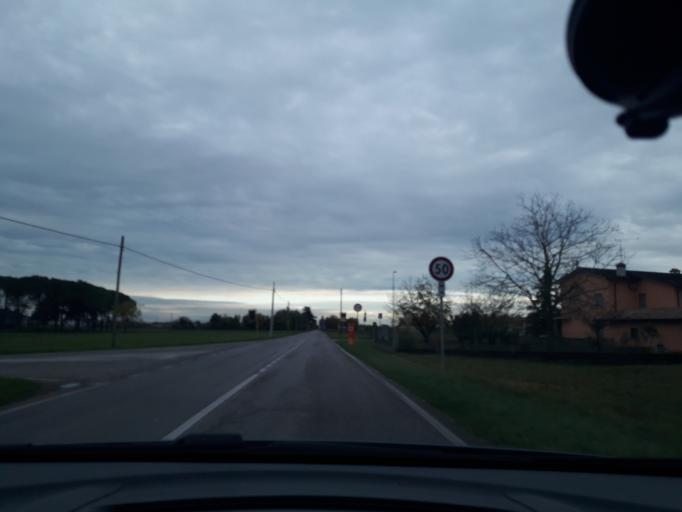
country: IT
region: Friuli Venezia Giulia
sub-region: Provincia di Udine
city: Tavagnacco
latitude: 46.1089
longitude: 13.2549
